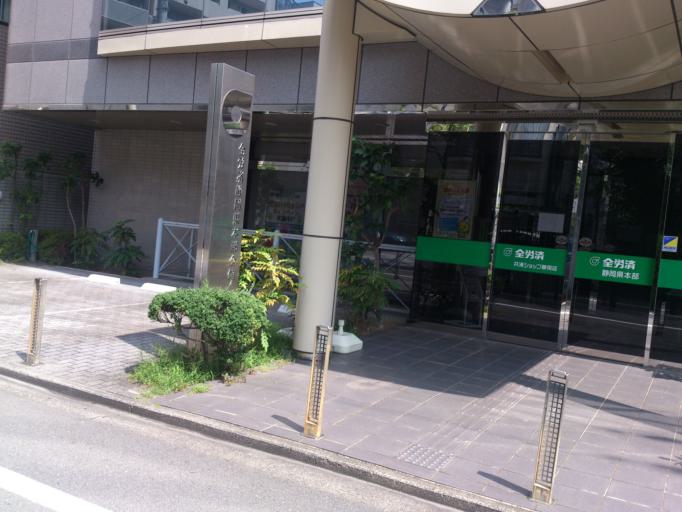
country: JP
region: Shizuoka
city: Shizuoka-shi
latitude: 34.9773
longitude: 138.3896
